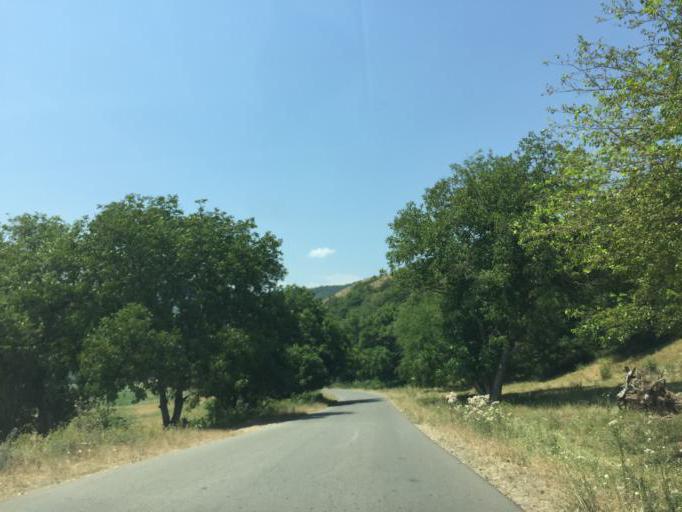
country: AZ
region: Tartar Rayon
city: Martakert
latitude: 40.1306
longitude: 46.4440
